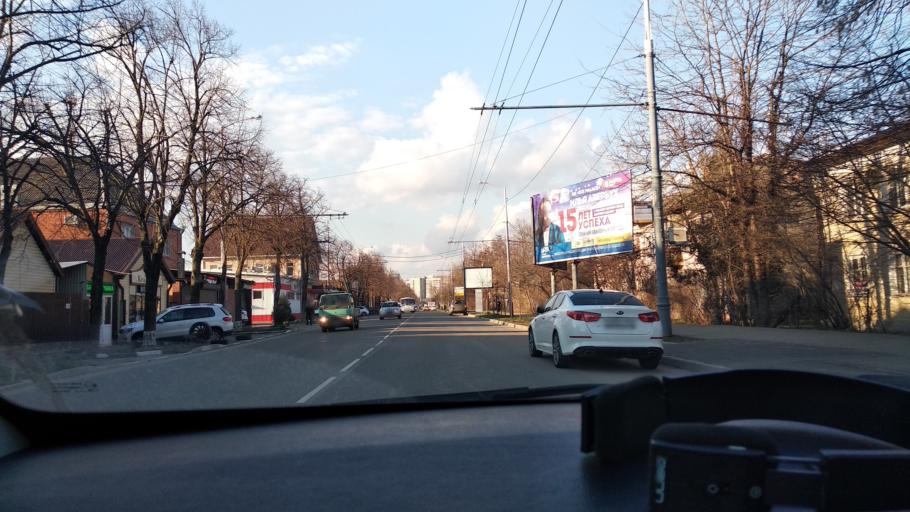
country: RU
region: Adygeya
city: Yablonovskiy
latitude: 45.0041
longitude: 38.9609
